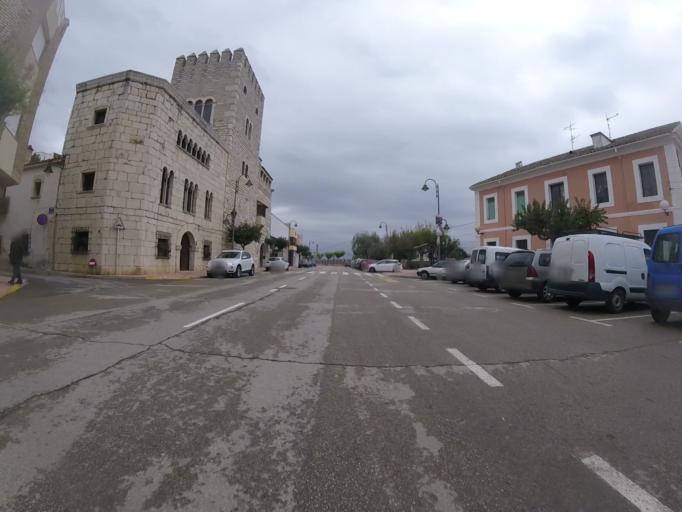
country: ES
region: Valencia
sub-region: Provincia de Castello
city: Alcala de Xivert
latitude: 40.3044
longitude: 0.2282
